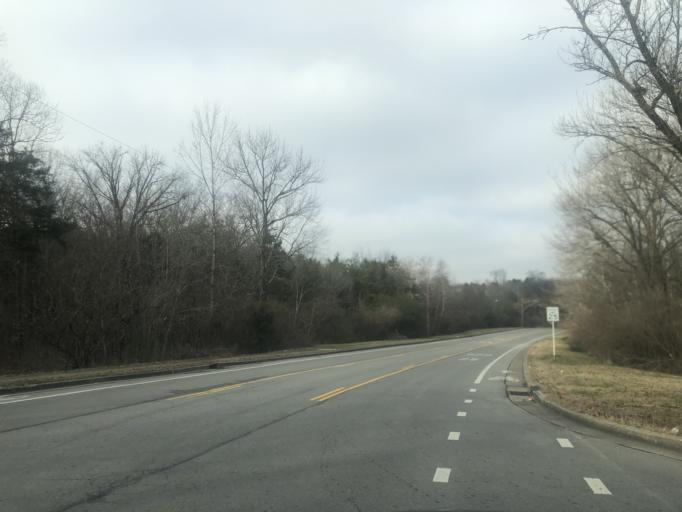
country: US
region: Tennessee
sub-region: Rutherford County
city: La Vergne
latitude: 36.0723
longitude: -86.6468
